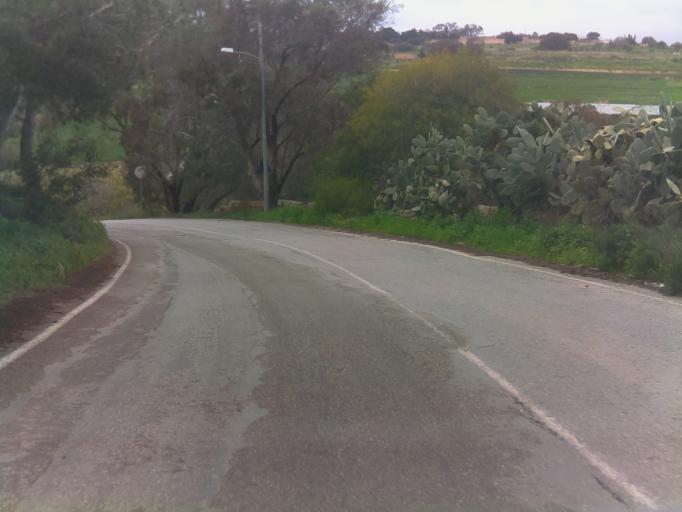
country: MT
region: Il-Mosta
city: Mosta
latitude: 35.9177
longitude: 14.4120
